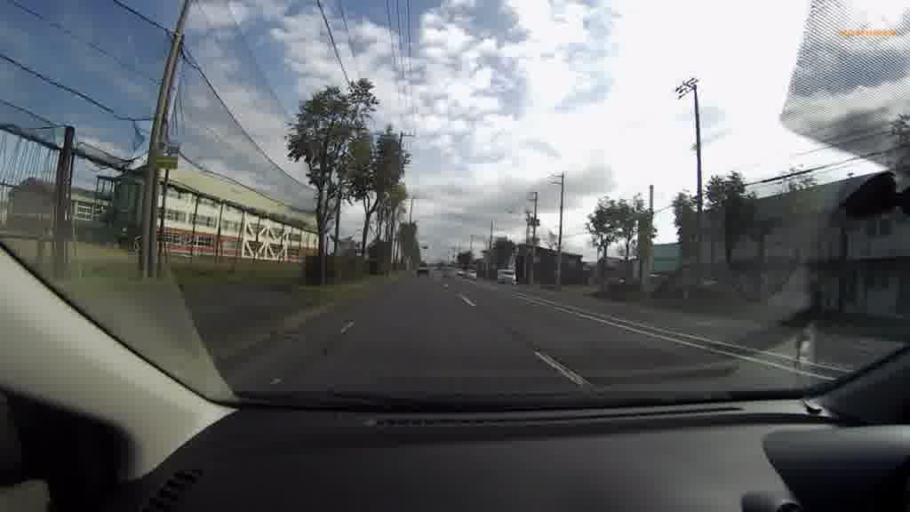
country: JP
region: Hokkaido
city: Kushiro
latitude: 43.0111
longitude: 144.2954
